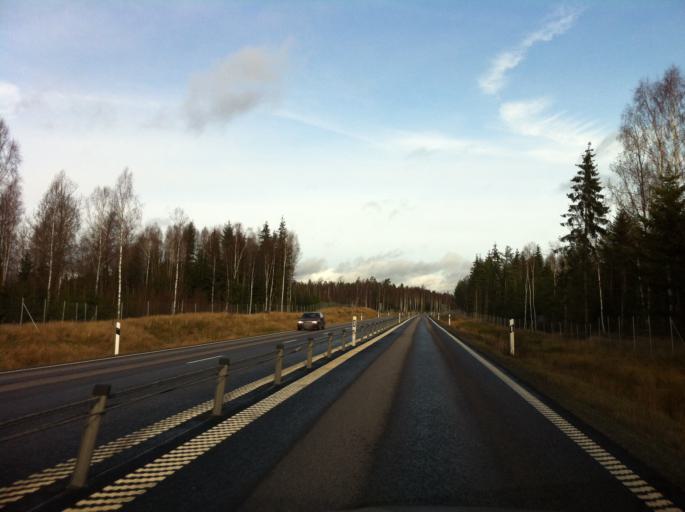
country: SE
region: Kronoberg
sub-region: Almhults Kommun
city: AElmhult
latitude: 56.6185
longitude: 14.2384
